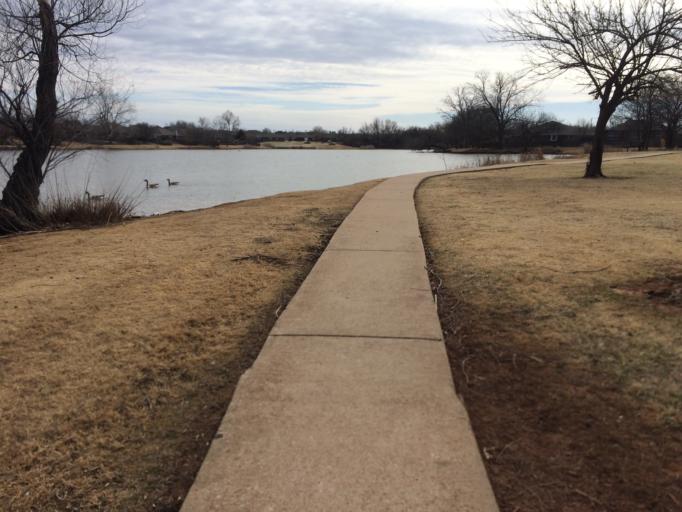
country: US
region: Oklahoma
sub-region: Cleveland County
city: Hall Park
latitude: 35.2246
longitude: -97.4026
